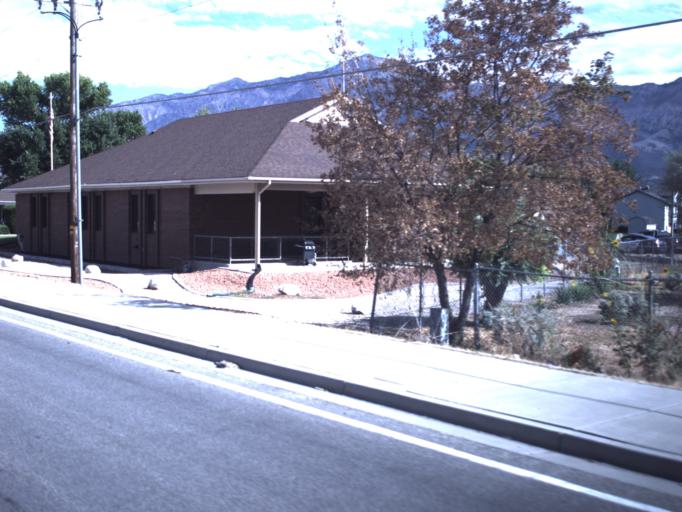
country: US
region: Utah
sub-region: Weber County
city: Harrisville
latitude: 41.2807
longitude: -111.9852
